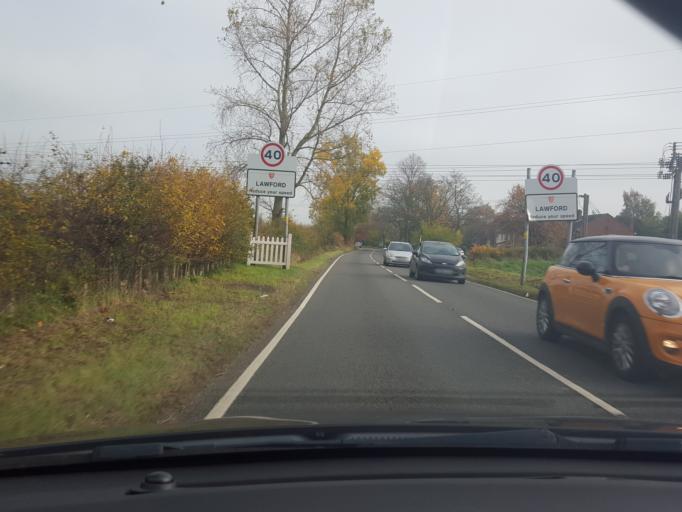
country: GB
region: England
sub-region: Essex
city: Manningtree
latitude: 51.9375
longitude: 1.0221
